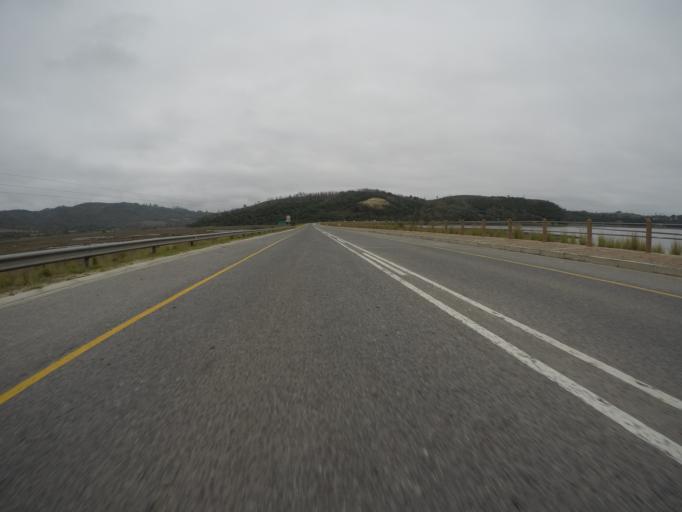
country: ZA
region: Western Cape
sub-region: Eden District Municipality
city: Knysna
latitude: -34.0302
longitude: 22.9923
